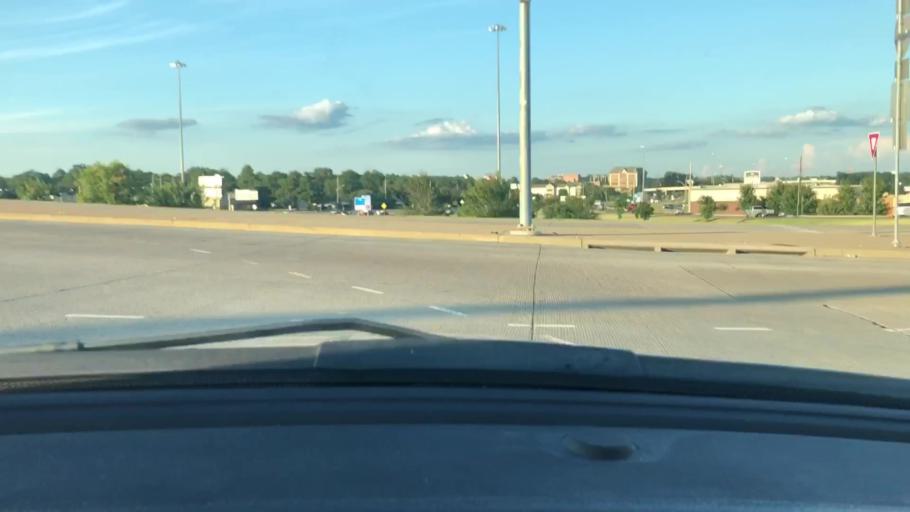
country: US
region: Texas
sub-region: Bowie County
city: Wake Village
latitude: 33.4553
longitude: -94.0857
